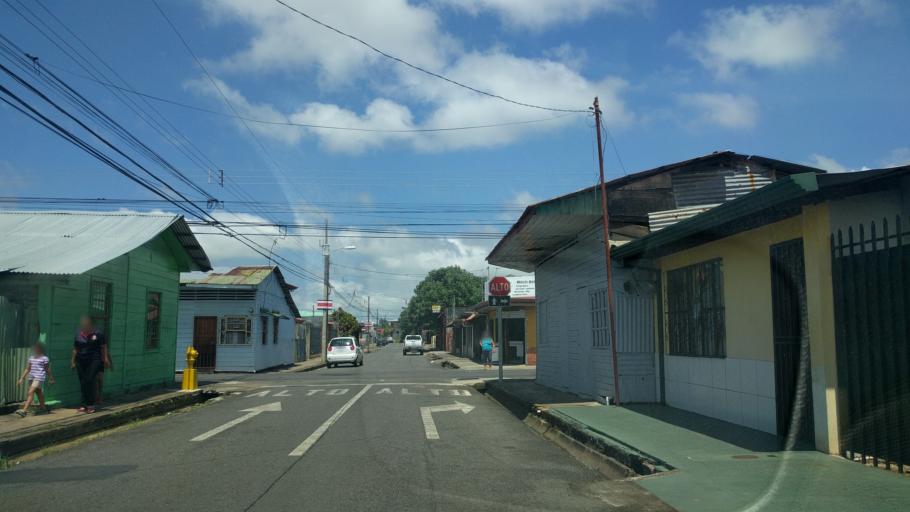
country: CR
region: Puntarenas
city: Esparza
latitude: 9.9935
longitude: -84.6646
